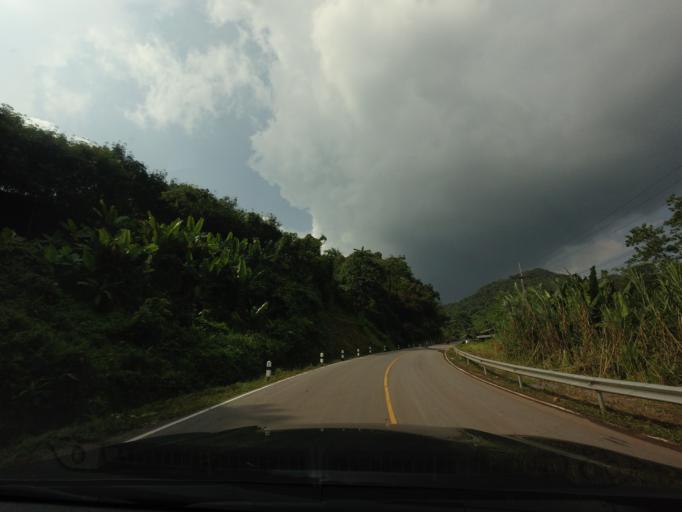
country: TH
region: Nan
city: Bo Kluea
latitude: 19.2350
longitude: 101.1821
